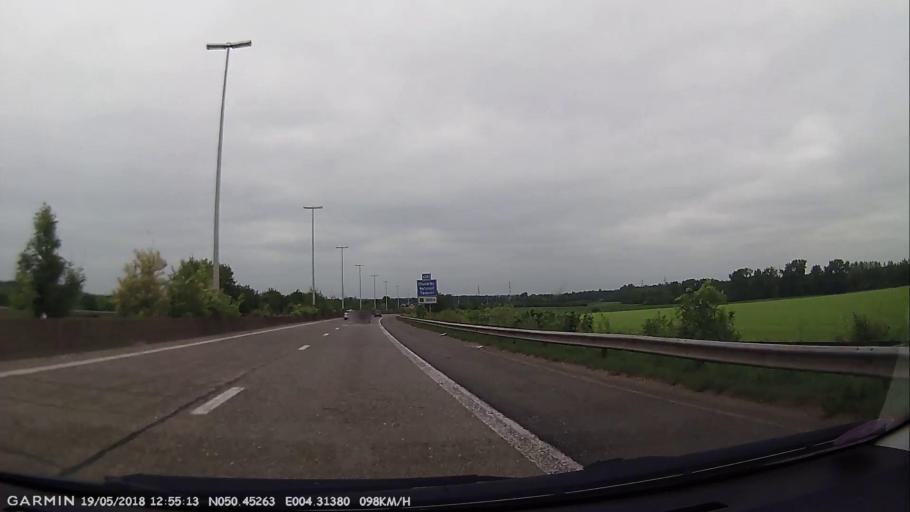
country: BE
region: Wallonia
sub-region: Province du Hainaut
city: Chapelle-lez-Herlaimont
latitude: 50.4530
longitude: 4.3135
